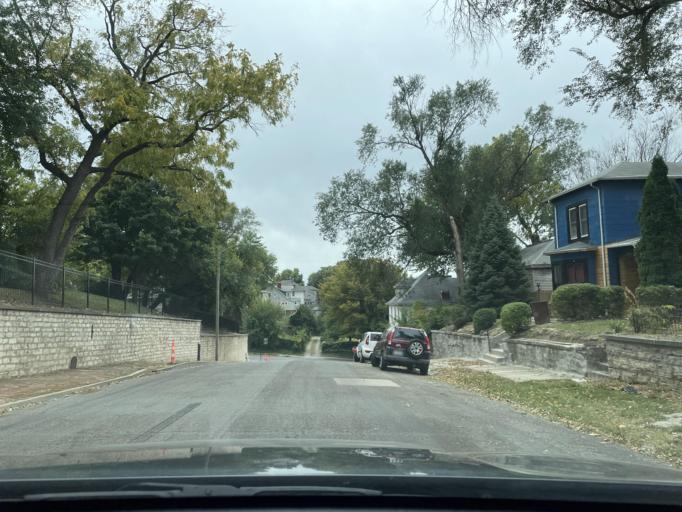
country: US
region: Missouri
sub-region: Buchanan County
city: Saint Joseph
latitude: 39.7632
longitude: -94.8454
